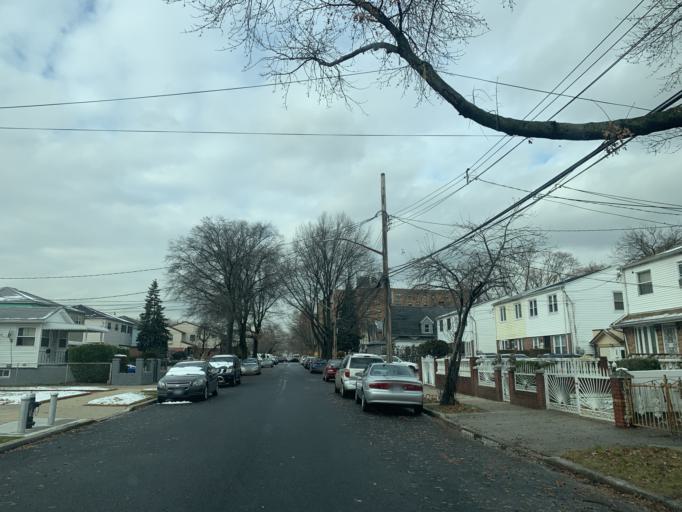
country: US
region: New York
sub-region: Queens County
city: Jamaica
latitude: 40.6888
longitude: -73.7825
